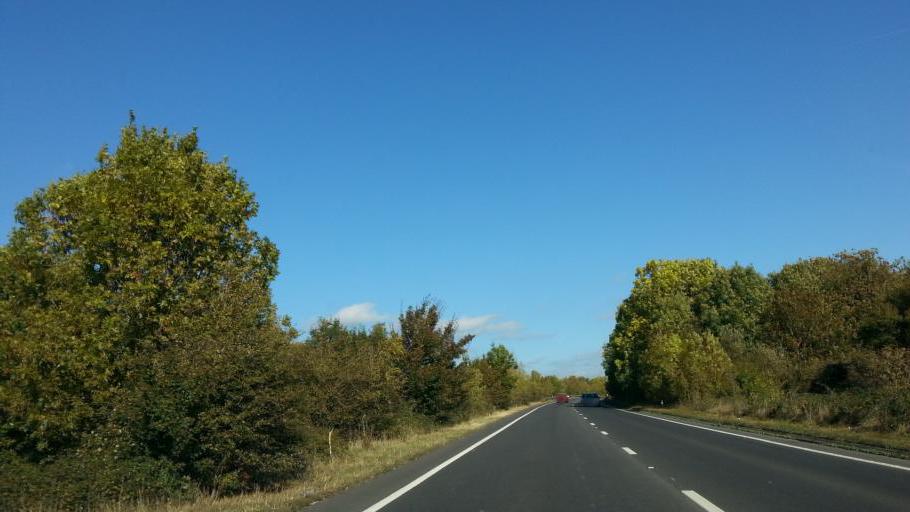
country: GB
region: England
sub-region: Northamptonshire
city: Stanwick
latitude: 52.3431
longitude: -0.5683
